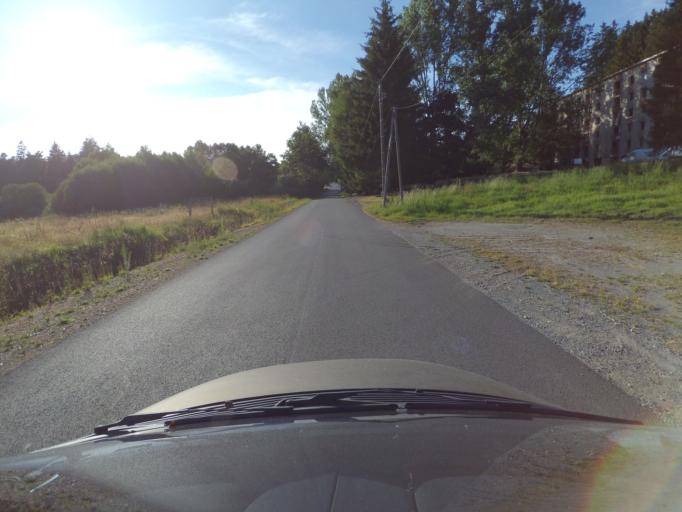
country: FR
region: Limousin
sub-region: Departement de la Correze
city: Bugeat
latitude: 45.7034
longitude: 2.0514
